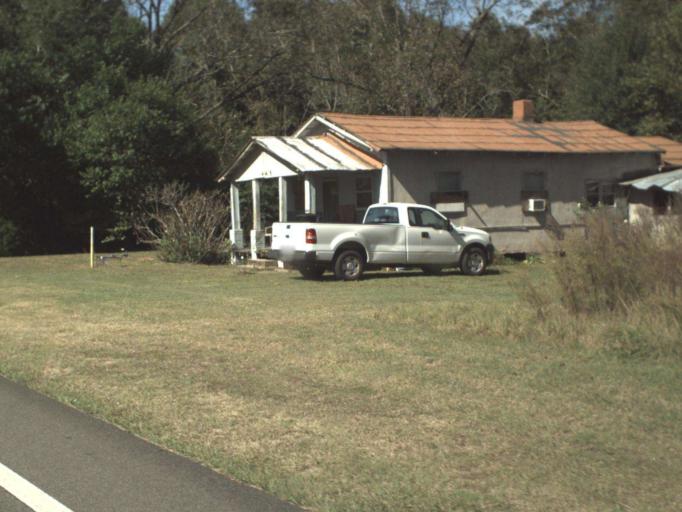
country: US
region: Florida
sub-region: Okaloosa County
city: Crestview
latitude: 30.7125
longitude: -86.7539
